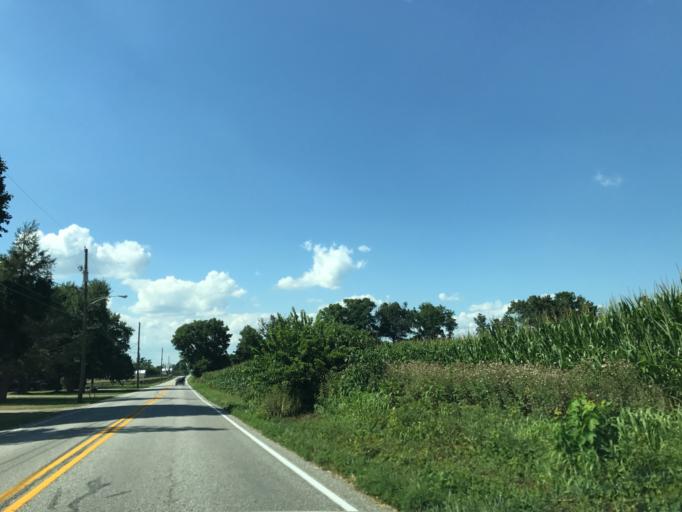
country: US
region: Pennsylvania
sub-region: York County
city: Pennville
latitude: 39.7754
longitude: -77.0257
